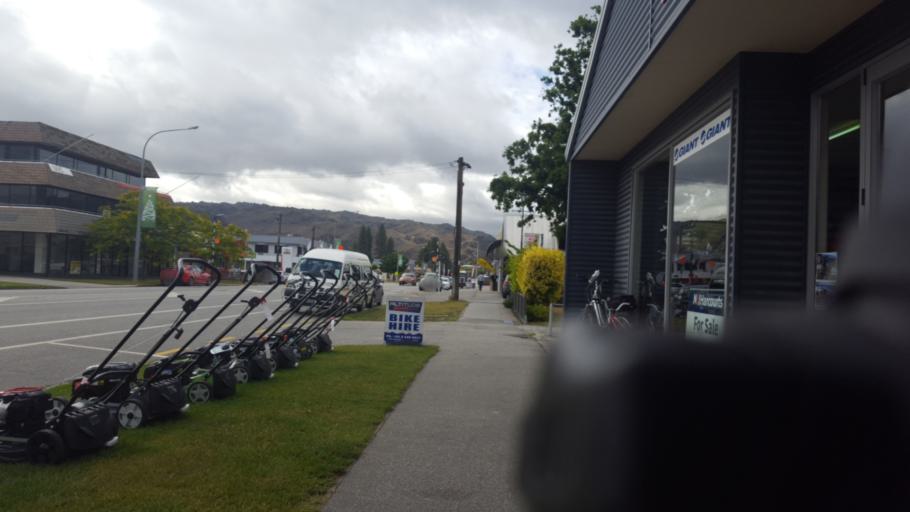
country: NZ
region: Otago
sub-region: Queenstown-Lakes District
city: Wanaka
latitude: -45.2505
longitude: 169.3869
